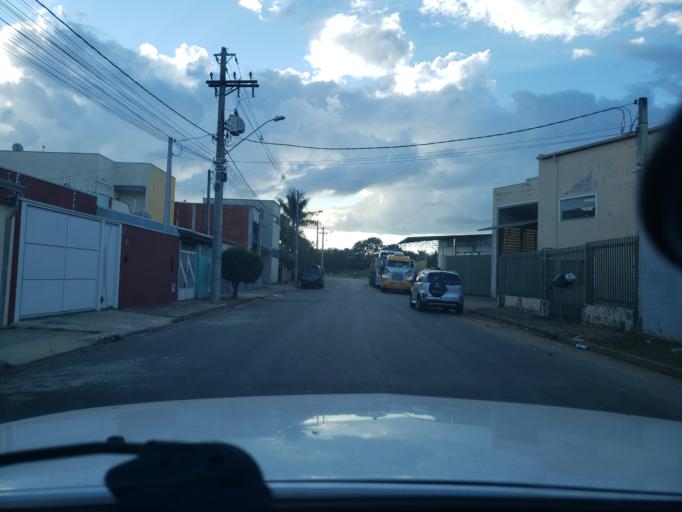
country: BR
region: Sao Paulo
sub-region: Moji-Guacu
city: Mogi-Gaucu
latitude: -22.3273
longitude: -46.9272
